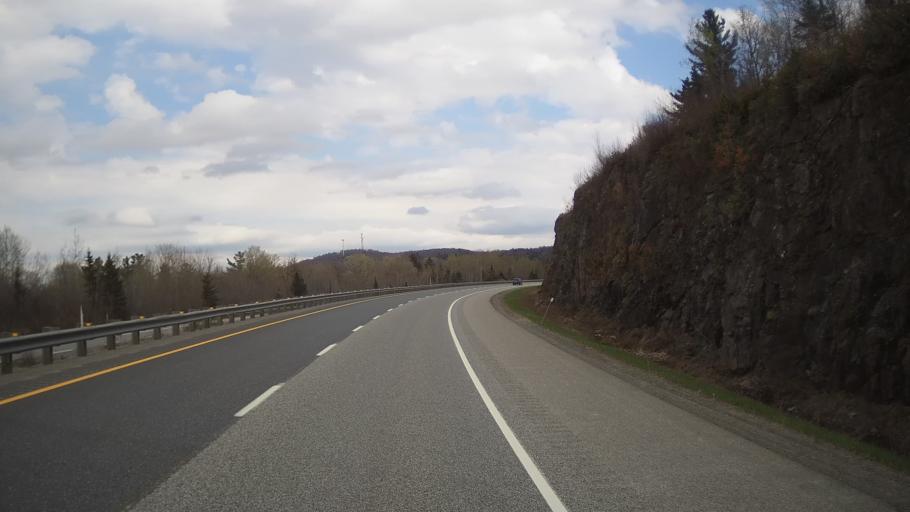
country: CA
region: Quebec
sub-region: Estrie
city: Magog
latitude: 45.2949
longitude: -72.2914
